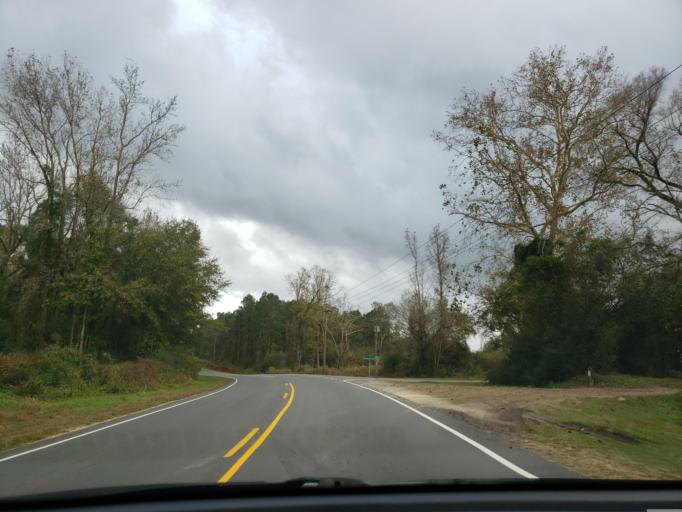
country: US
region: North Carolina
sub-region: Duplin County
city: Kenansville
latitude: 34.8737
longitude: -77.8913
